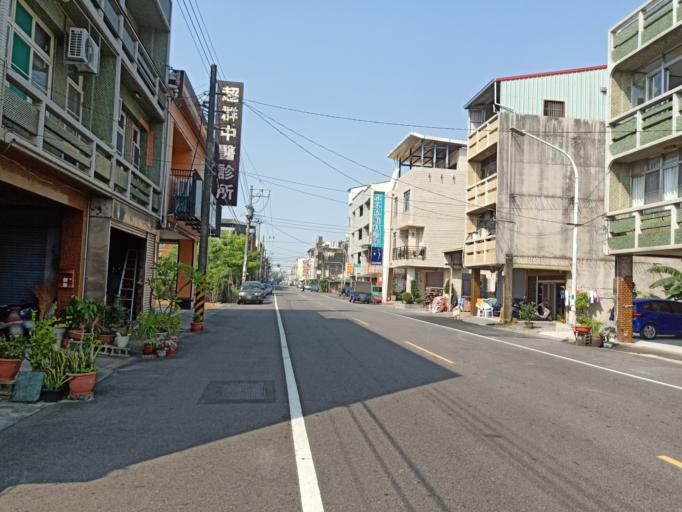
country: TW
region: Taiwan
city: Yujing
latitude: 23.1316
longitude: 120.3002
